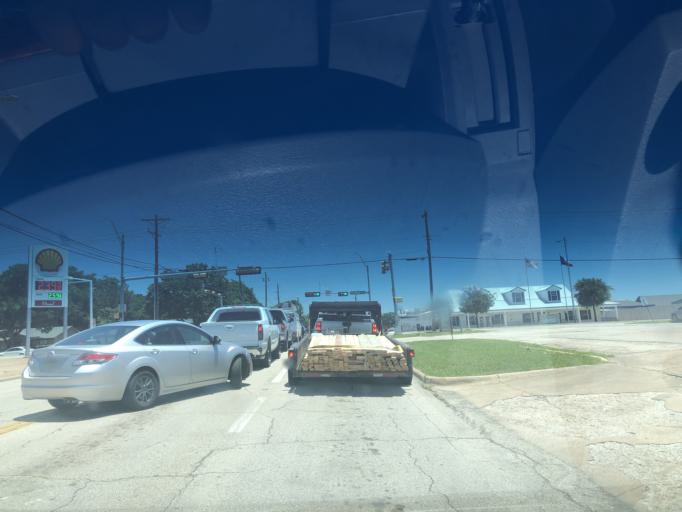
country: US
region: Texas
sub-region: Dallas County
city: Grand Prairie
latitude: 32.7203
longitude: -97.0156
